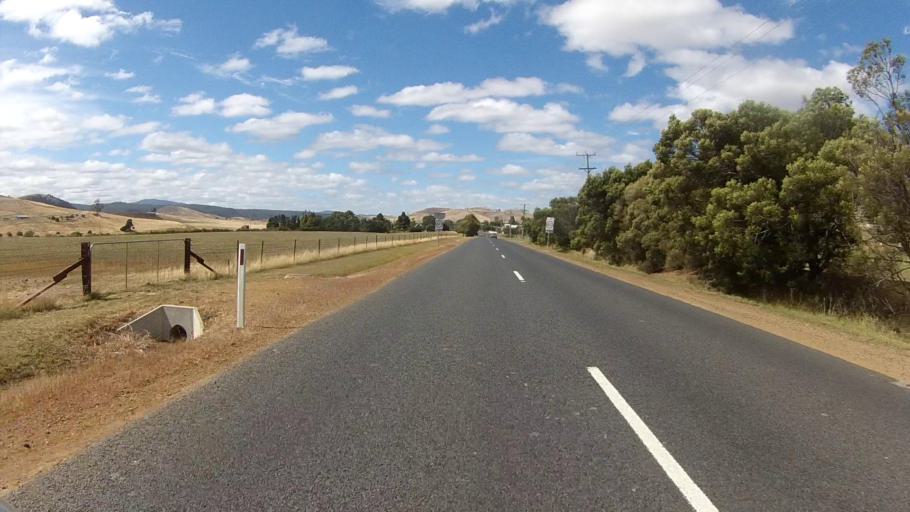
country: AU
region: Tasmania
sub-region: Brighton
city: Bridgewater
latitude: -42.5299
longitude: 147.3609
